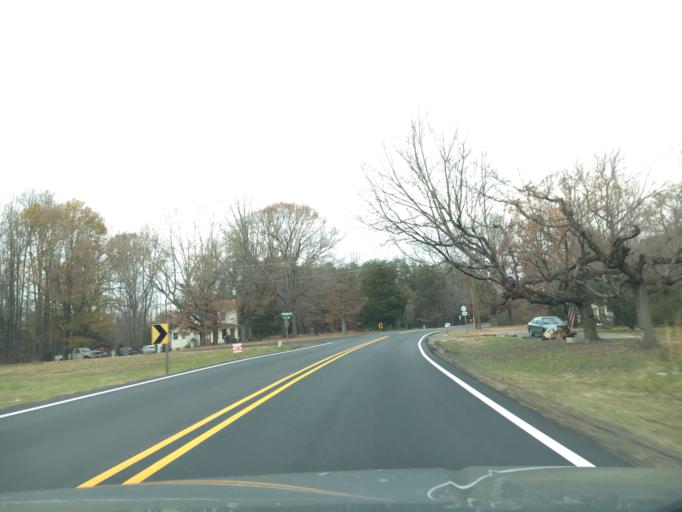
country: US
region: Virginia
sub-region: Cumberland County
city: Cumberland
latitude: 37.4721
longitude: -78.2816
